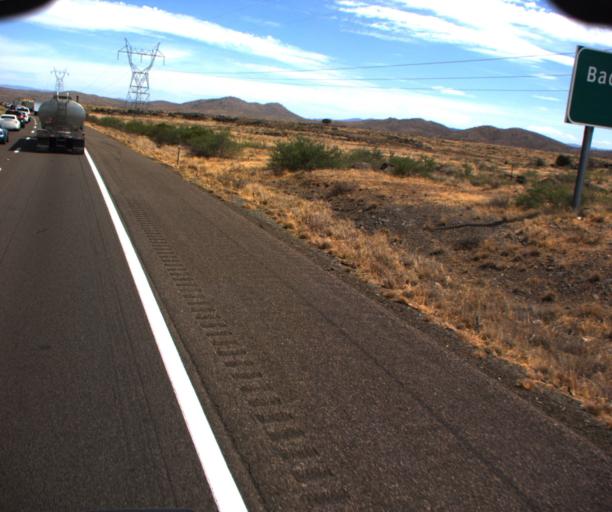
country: US
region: Arizona
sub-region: Yavapai County
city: Cordes Lakes
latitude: 34.2196
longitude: -112.1106
